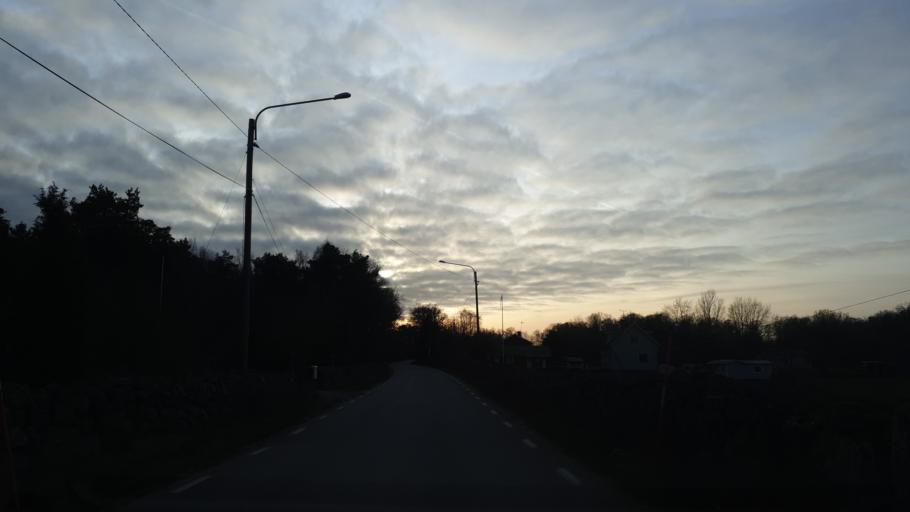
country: SE
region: Blekinge
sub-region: Karlskrona Kommun
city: Jaemjoe
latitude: 56.1490
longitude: 15.9012
